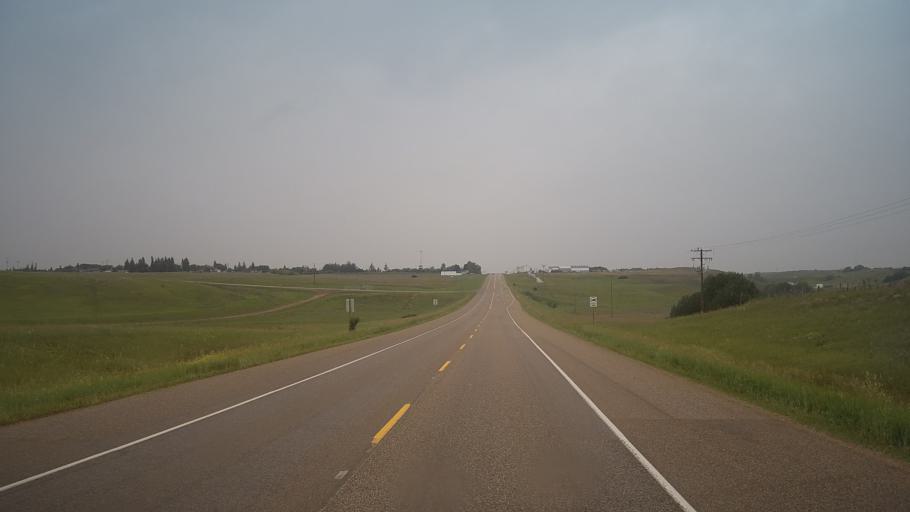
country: CA
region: Saskatchewan
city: Biggar
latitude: 52.0585
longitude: -107.9602
